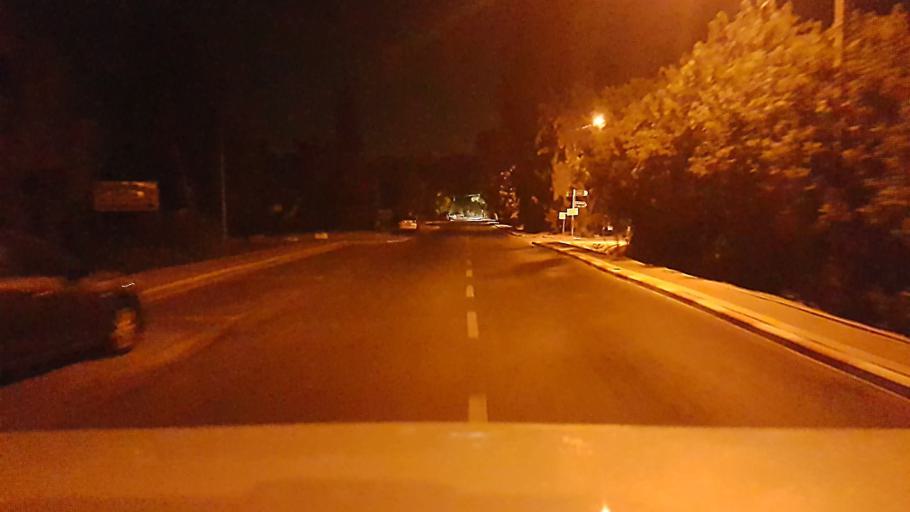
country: IL
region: Central District
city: Nehalim
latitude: 32.0767
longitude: 34.9165
